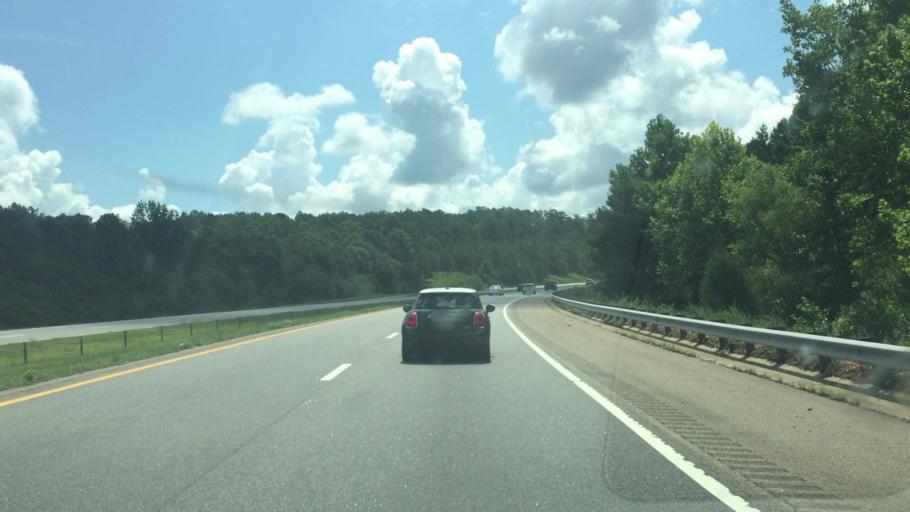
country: US
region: North Carolina
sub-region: Richmond County
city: Cordova
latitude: 34.9466
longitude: -79.8492
